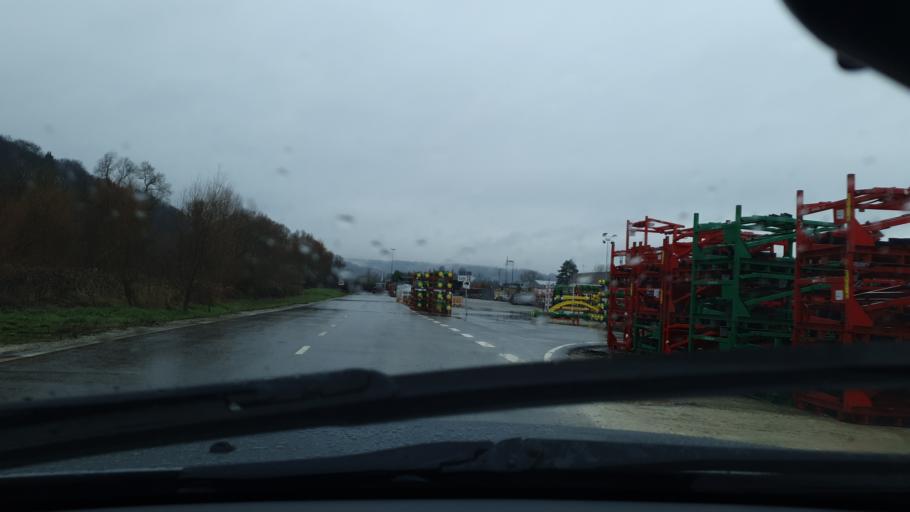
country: DE
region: Rheinland-Pfalz
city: Zweibrucken
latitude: 49.2574
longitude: 7.3321
